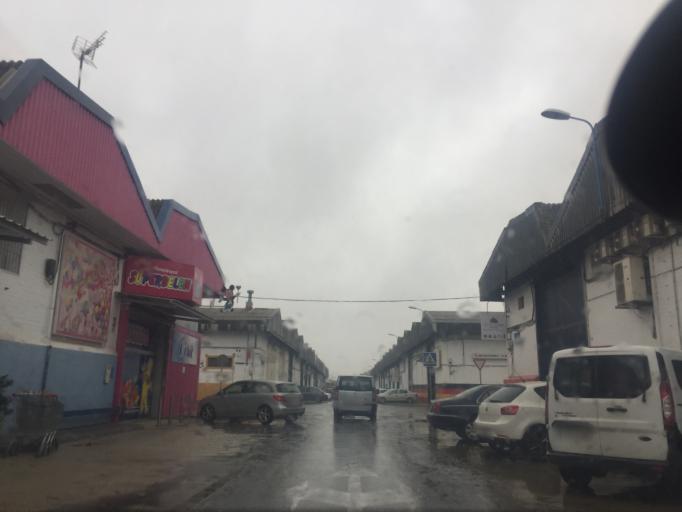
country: ES
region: Andalusia
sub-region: Provincia de Sevilla
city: Sevilla
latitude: 37.3679
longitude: -5.9583
